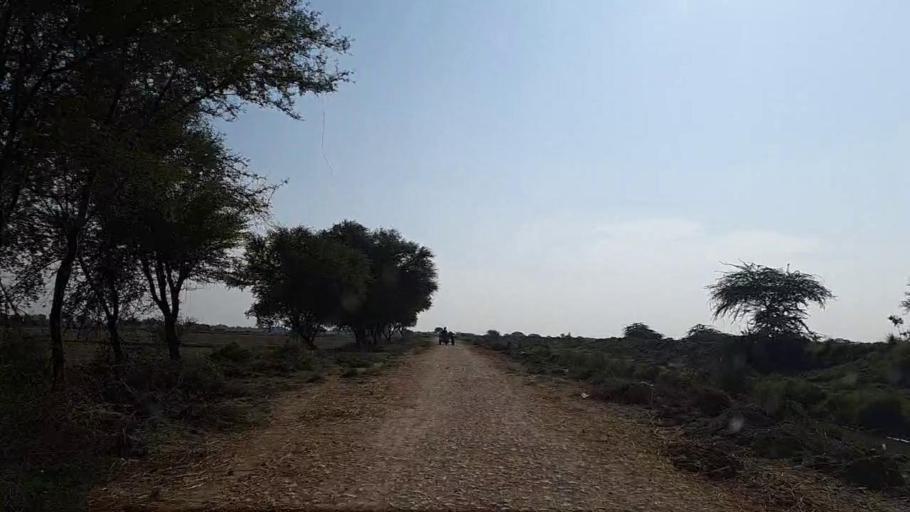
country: PK
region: Sindh
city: Daro Mehar
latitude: 24.7288
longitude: 68.1159
